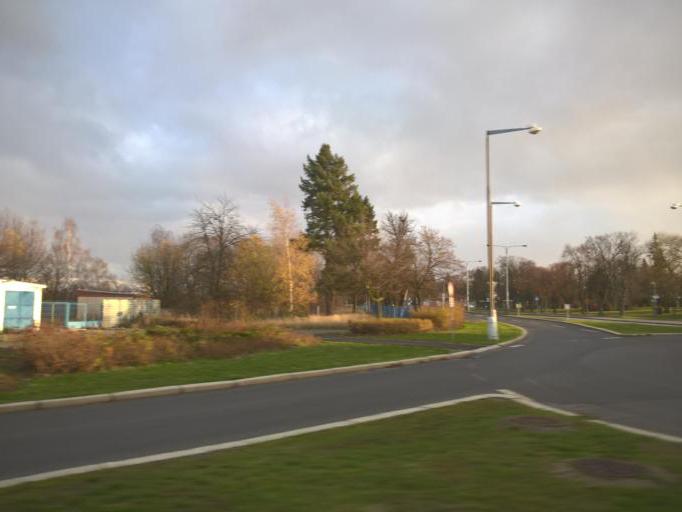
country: CZ
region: Central Bohemia
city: Hostivice
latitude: 50.1000
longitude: 14.2875
